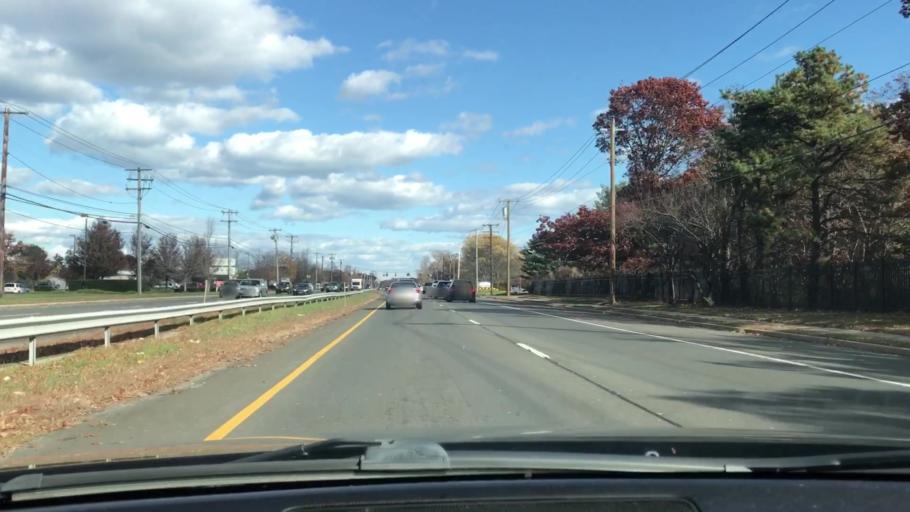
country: US
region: New York
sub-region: Suffolk County
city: Terryville
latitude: 40.9027
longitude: -73.0751
